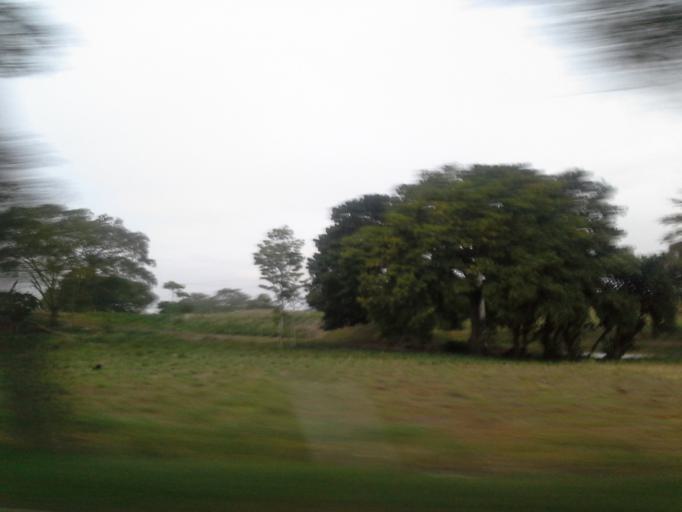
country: CO
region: Sucre
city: Los Palmitos
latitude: 9.3600
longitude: -75.2807
